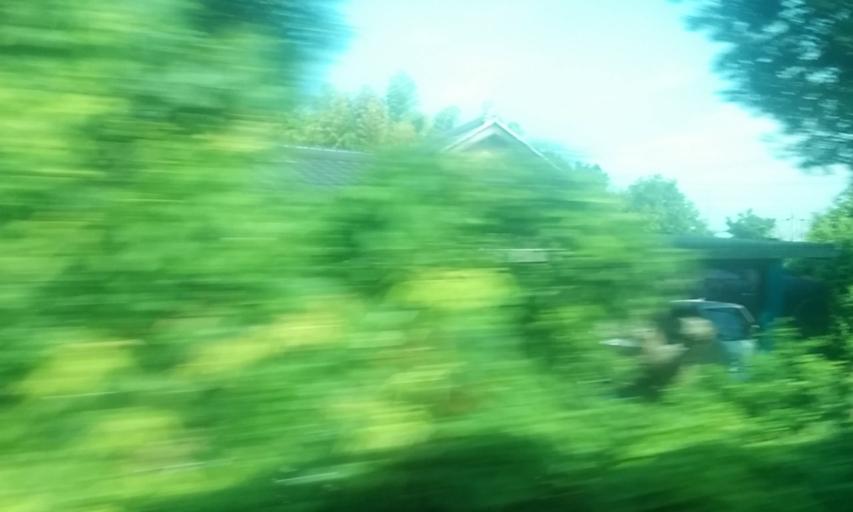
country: JP
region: Saitama
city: Kukichuo
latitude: 36.0470
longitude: 139.6733
